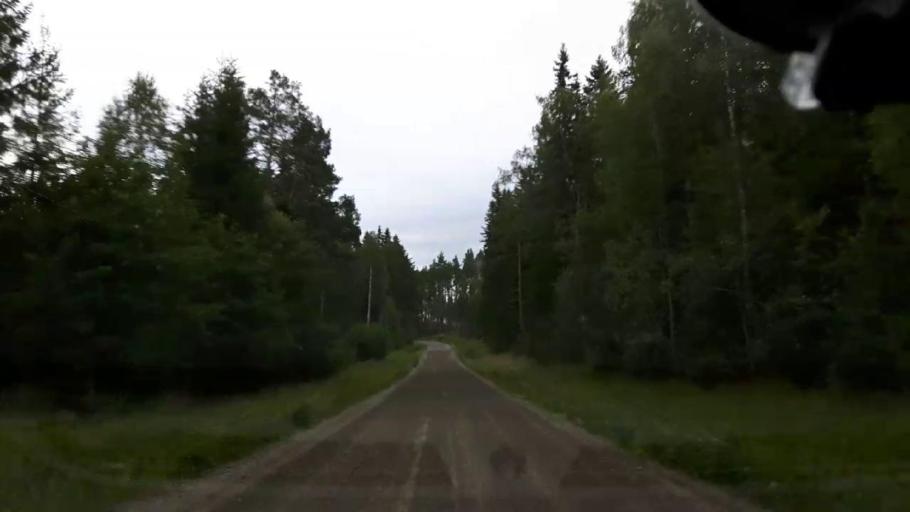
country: SE
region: Jaemtland
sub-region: Braecke Kommun
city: Braecke
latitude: 62.8929
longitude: 15.6052
